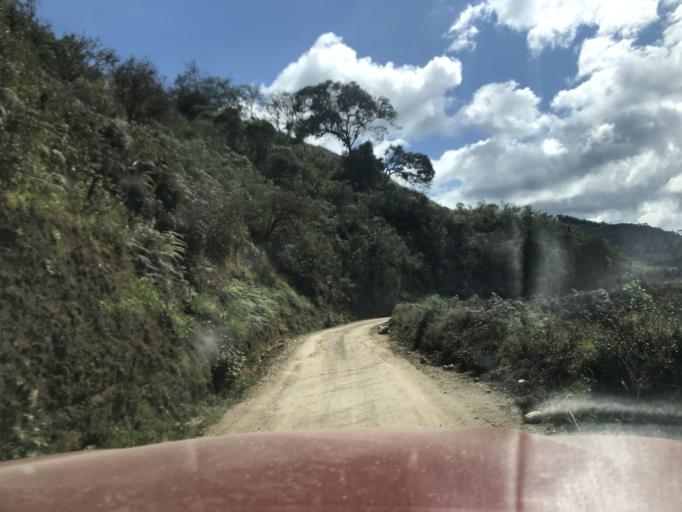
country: PE
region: Cajamarca
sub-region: Provincia de Chota
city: Querocoto
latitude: -6.3501
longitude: -79.0383
